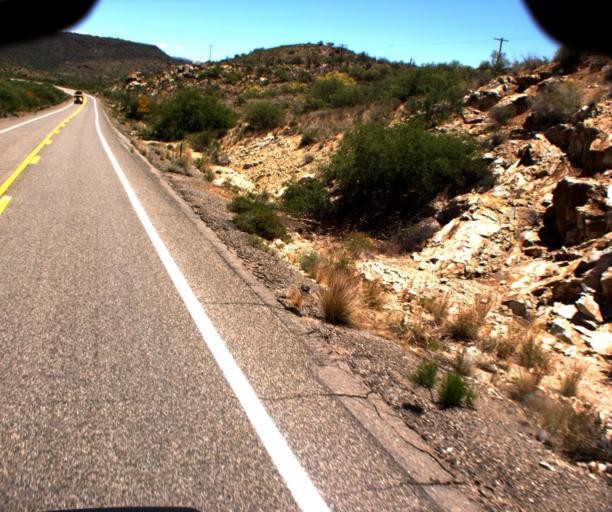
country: US
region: Arizona
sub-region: Yavapai County
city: Bagdad
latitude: 34.5176
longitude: -113.0915
